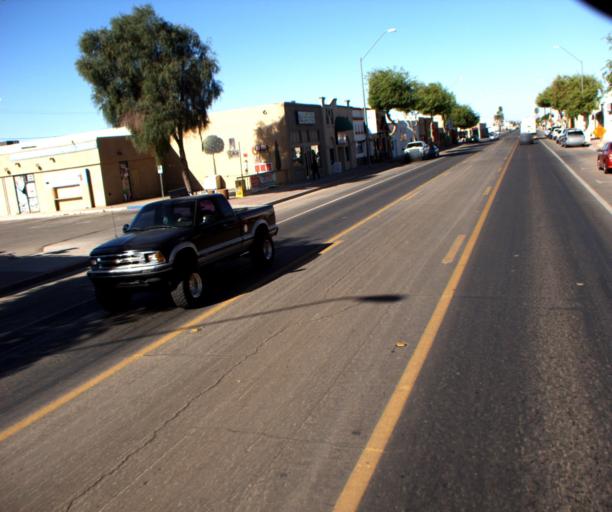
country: US
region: Arizona
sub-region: Yuma County
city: Somerton
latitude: 32.5967
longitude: -114.7115
